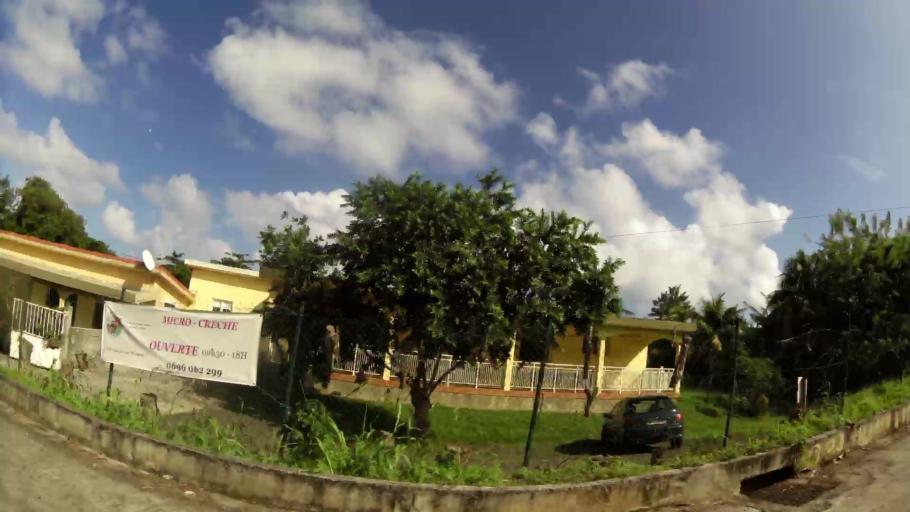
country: MQ
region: Martinique
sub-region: Martinique
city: Sainte-Marie
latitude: 14.7949
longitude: -61.0027
